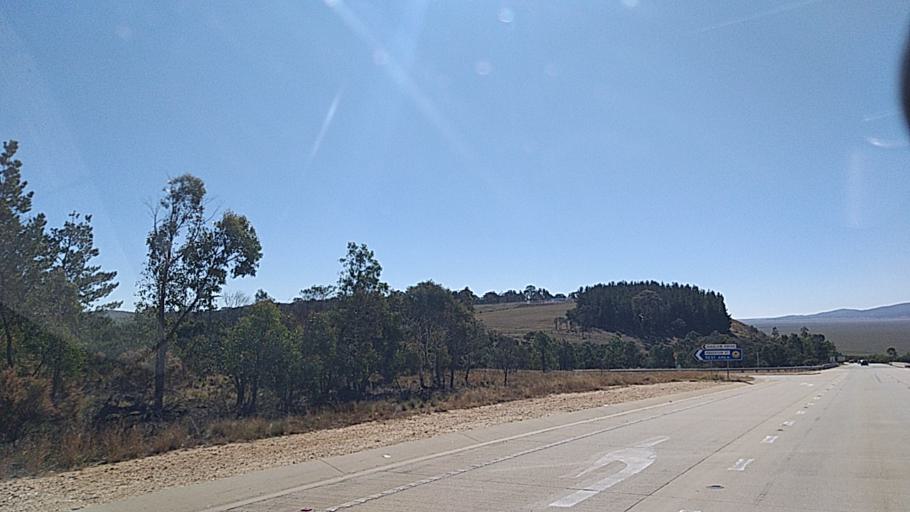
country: AU
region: New South Wales
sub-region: Yass Valley
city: Gundaroo
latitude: -35.1017
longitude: 149.3739
